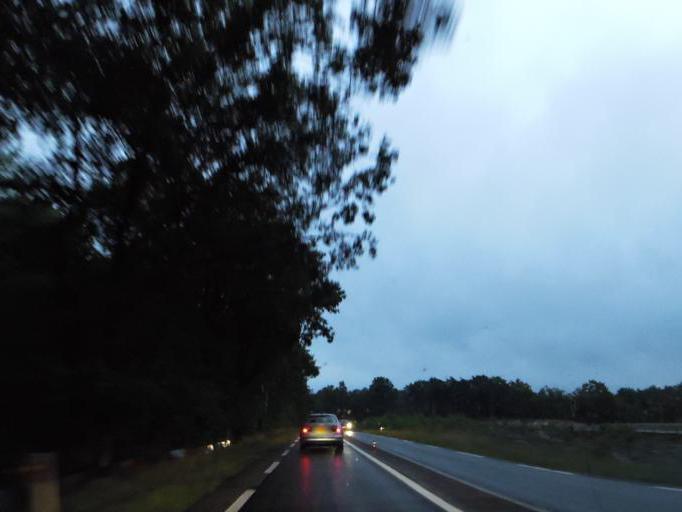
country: NL
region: Limburg
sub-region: Gemeente Brunssum
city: Brunssum
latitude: 50.9289
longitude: 6.0097
